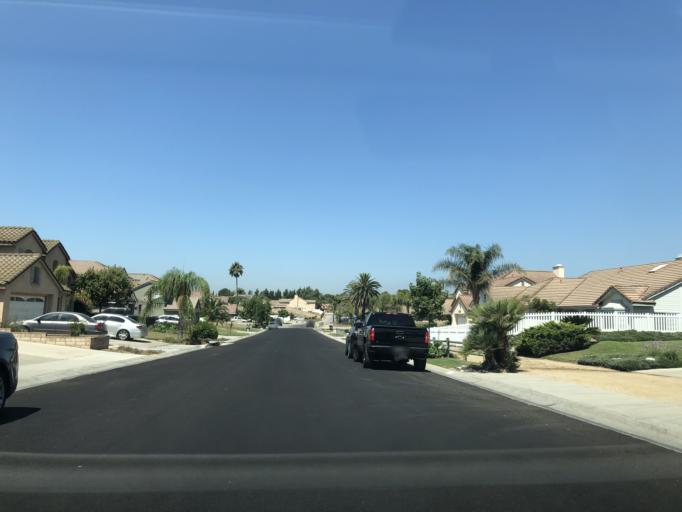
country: US
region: California
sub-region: Riverside County
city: Norco
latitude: 33.9139
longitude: -117.5776
